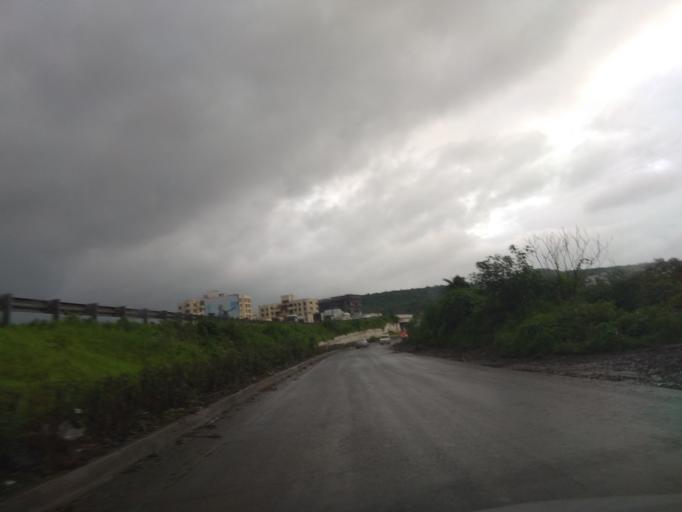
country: IN
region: Maharashtra
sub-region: Pune Division
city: Kharakvasla
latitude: 18.4909
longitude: 73.7909
